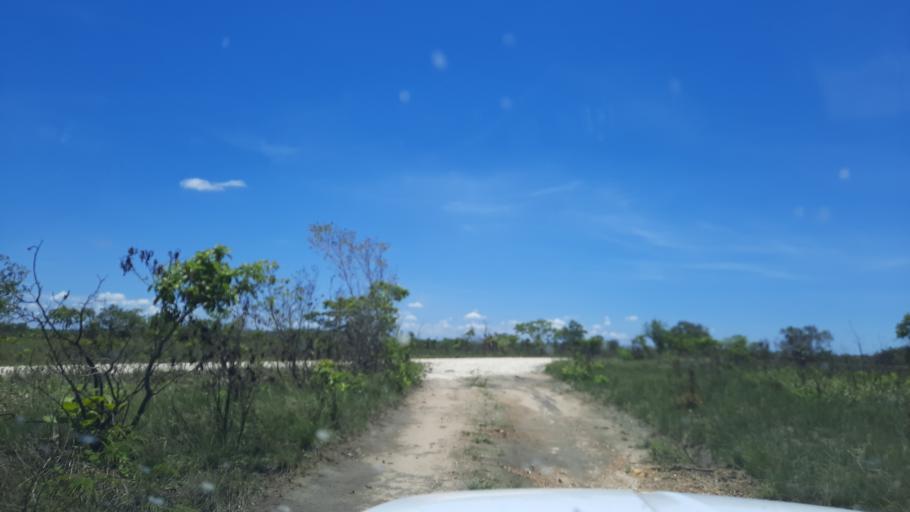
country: BZ
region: Cayo
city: Belmopan
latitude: 17.3850
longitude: -88.4949
